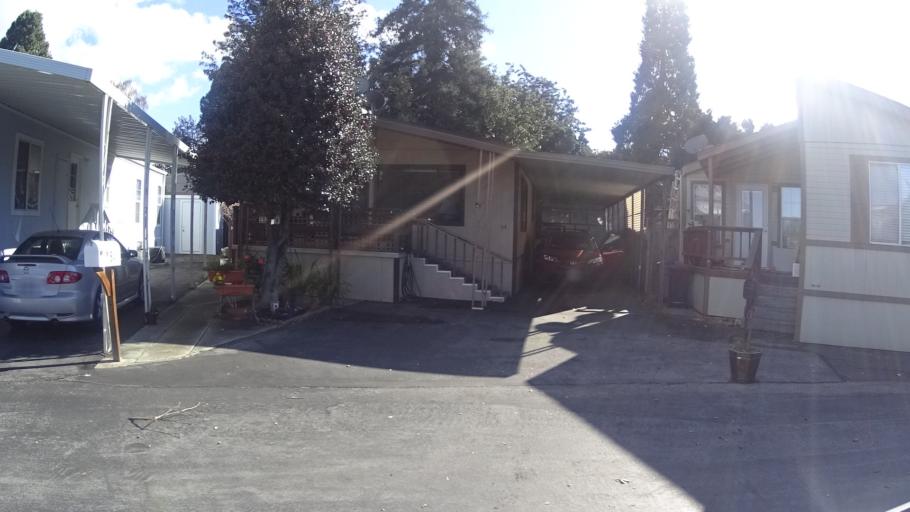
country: US
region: California
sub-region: Santa Clara County
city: Mountain View
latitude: 37.3794
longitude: -122.0664
